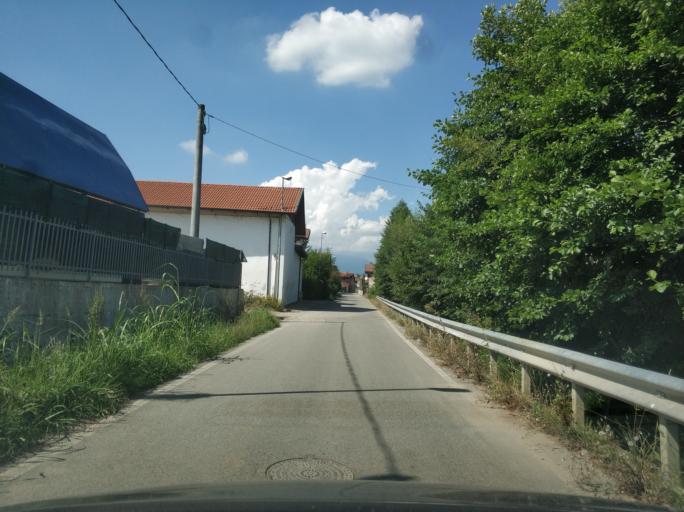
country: IT
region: Piedmont
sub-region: Provincia di Torino
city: Rivarolo Canavese
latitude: 45.3134
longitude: 7.7231
